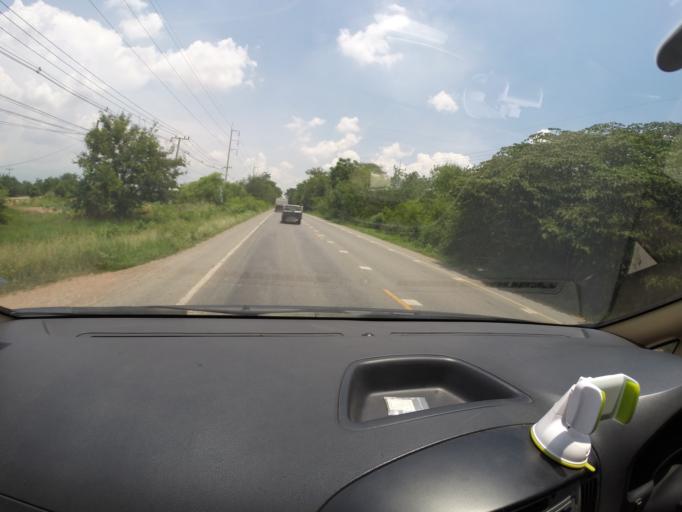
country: TH
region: Nakhon Ratchasima
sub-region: Amphoe Thepharak
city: Thepharak
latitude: 15.1281
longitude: 101.5594
